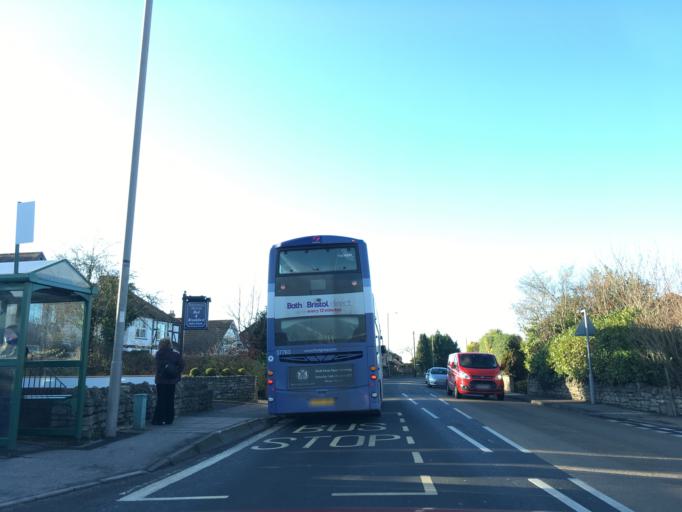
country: GB
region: England
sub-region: Bath and North East Somerset
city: Saltford
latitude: 51.4022
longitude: -2.4585
